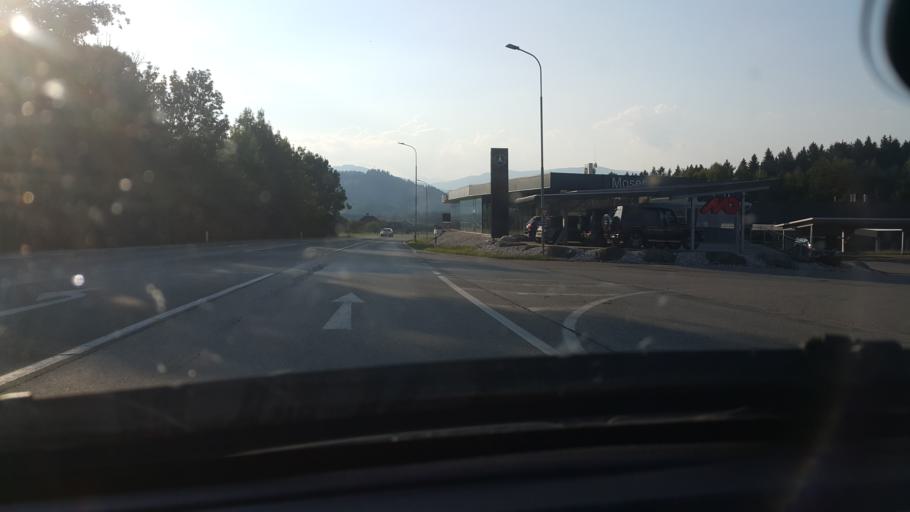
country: AT
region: Carinthia
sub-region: Politischer Bezirk Feldkirchen
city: Feldkirchen in Karnten
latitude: 46.6931
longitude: 14.1269
